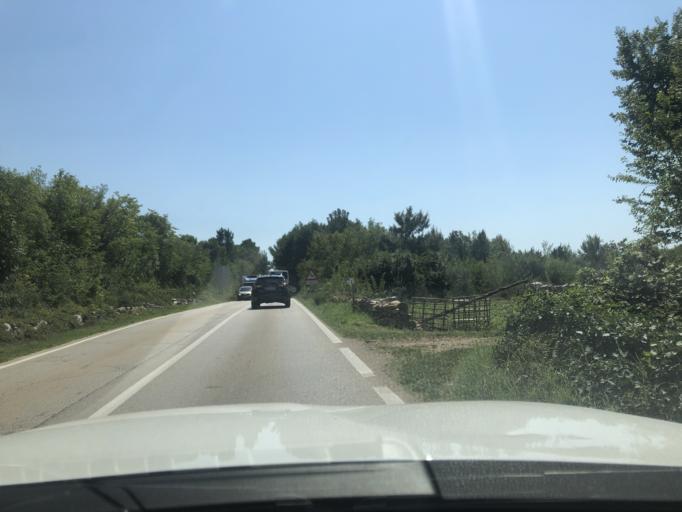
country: HR
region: Istarska
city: Vodnjan
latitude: 45.0350
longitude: 13.7909
